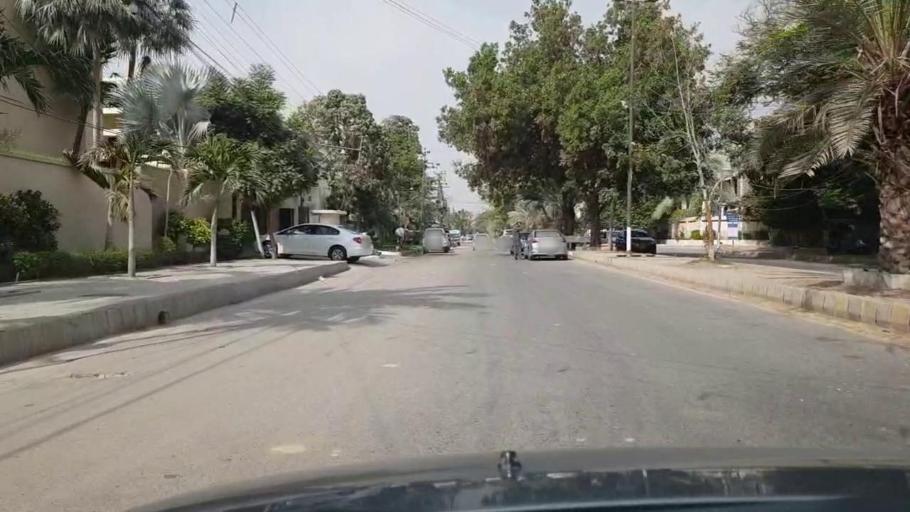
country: PK
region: Sindh
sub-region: Karachi District
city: Karachi
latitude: 24.8725
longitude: 67.0879
